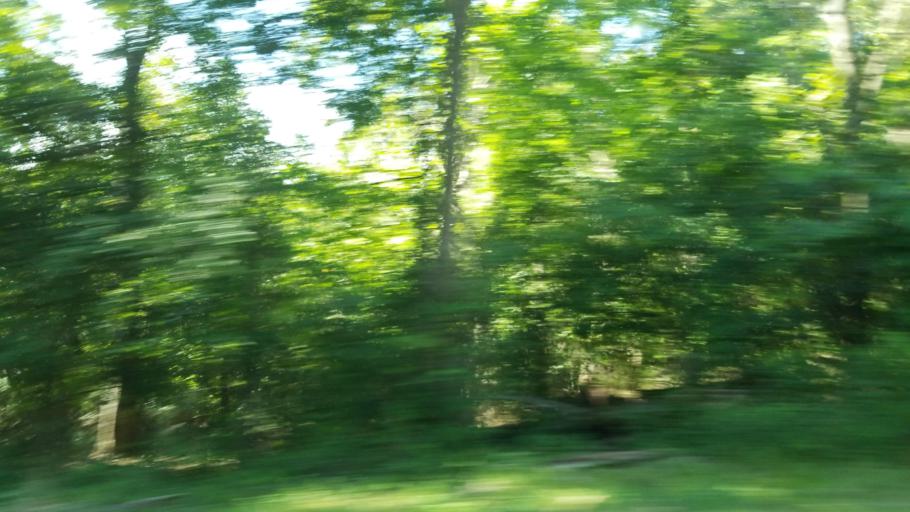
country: US
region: Illinois
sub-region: Saline County
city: Carrier Mills
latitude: 37.8006
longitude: -88.7354
